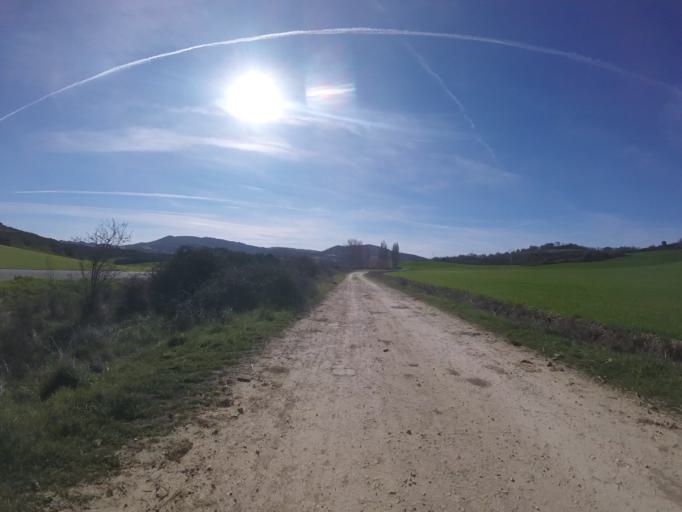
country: ES
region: Navarre
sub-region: Provincia de Navarra
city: Yerri
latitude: 42.6783
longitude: -1.9584
